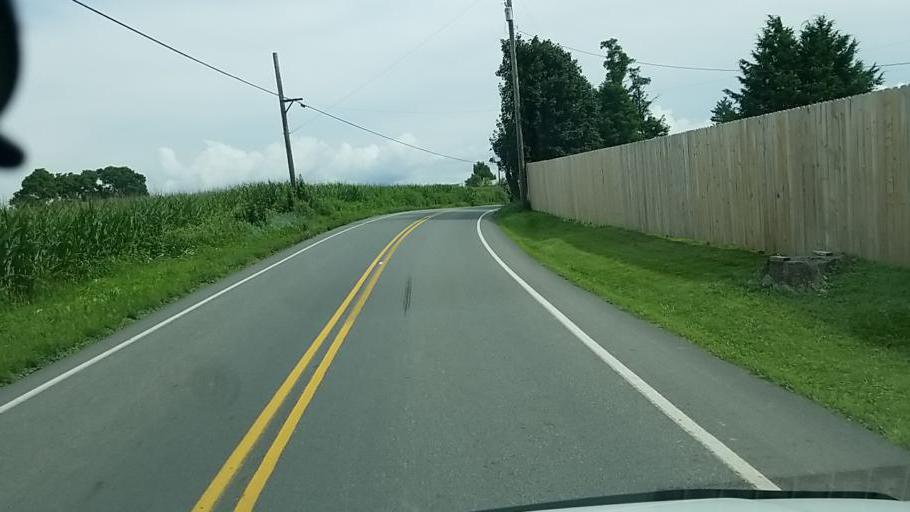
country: US
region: Pennsylvania
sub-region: Dauphin County
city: Elizabethville
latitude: 40.6118
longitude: -76.7812
